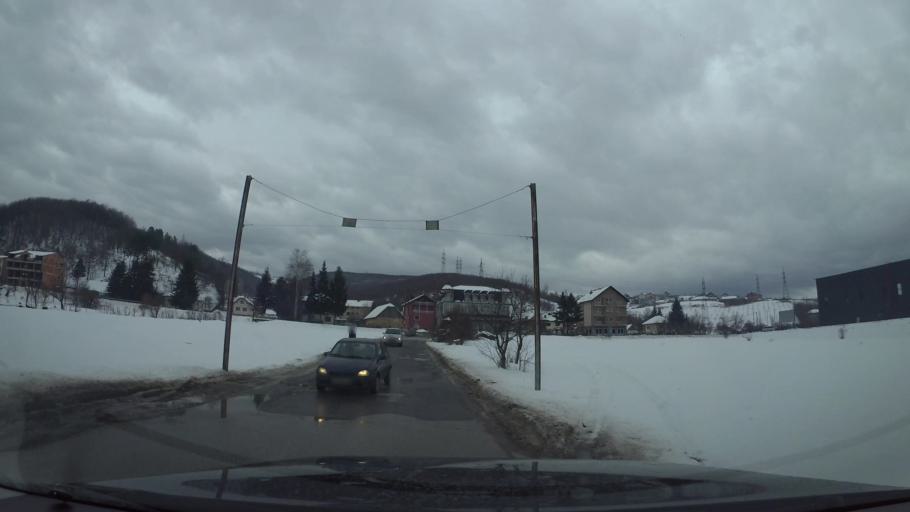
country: BA
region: Federation of Bosnia and Herzegovina
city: Vogosca
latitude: 43.8846
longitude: 18.3207
